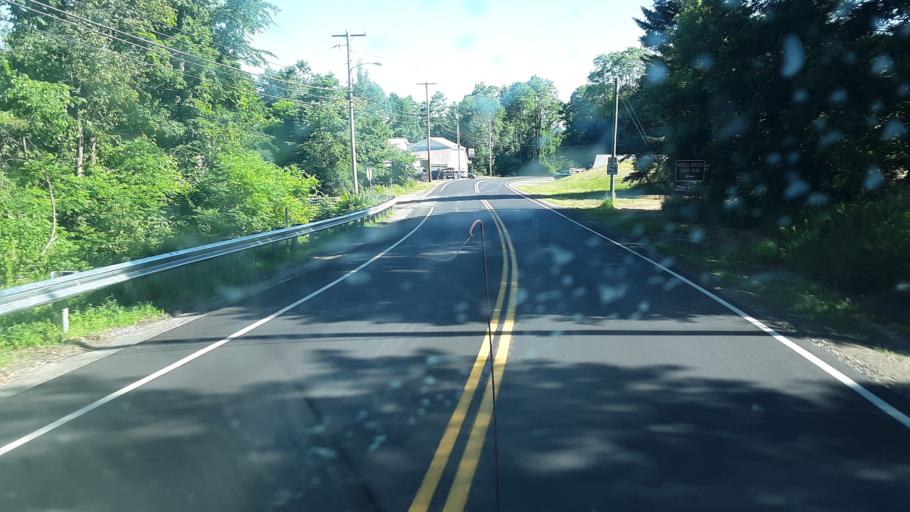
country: US
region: New Hampshire
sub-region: Grafton County
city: Haverhill
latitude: 44.0401
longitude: -72.0591
